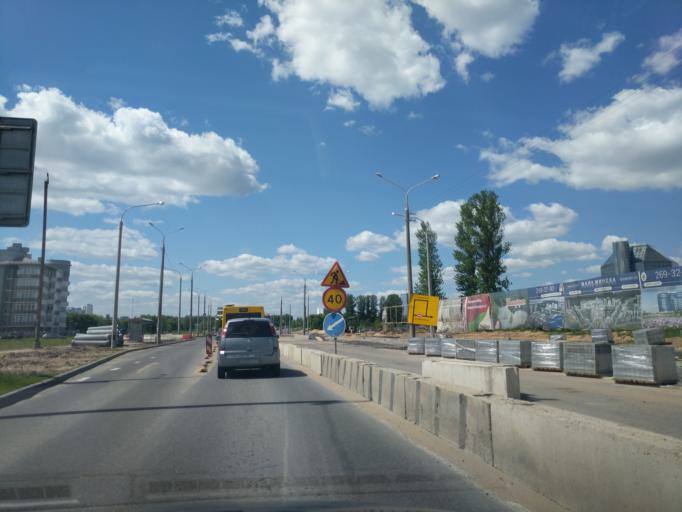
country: BY
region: Minsk
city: Borovlyany
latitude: 53.9272
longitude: 27.6521
